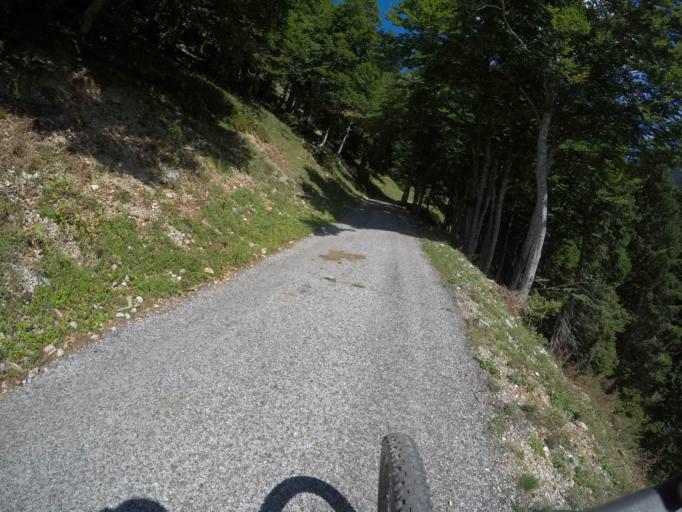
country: IT
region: Friuli Venezia Giulia
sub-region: Provincia di Udine
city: Ligosullo
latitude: 46.5027
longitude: 13.0685
